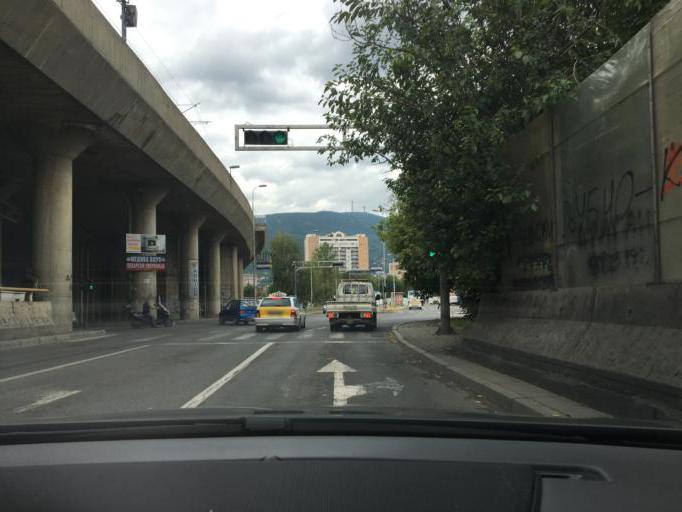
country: MK
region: Karpos
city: Skopje
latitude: 41.9932
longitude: 21.4478
